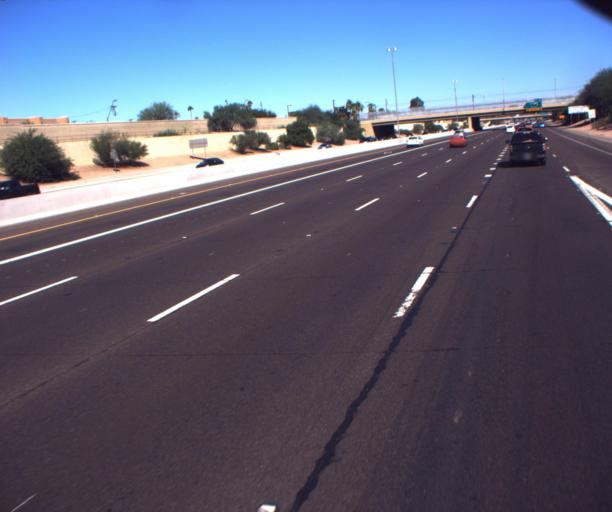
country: US
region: Arizona
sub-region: Maricopa County
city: Tempe
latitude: 33.4126
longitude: -111.8911
